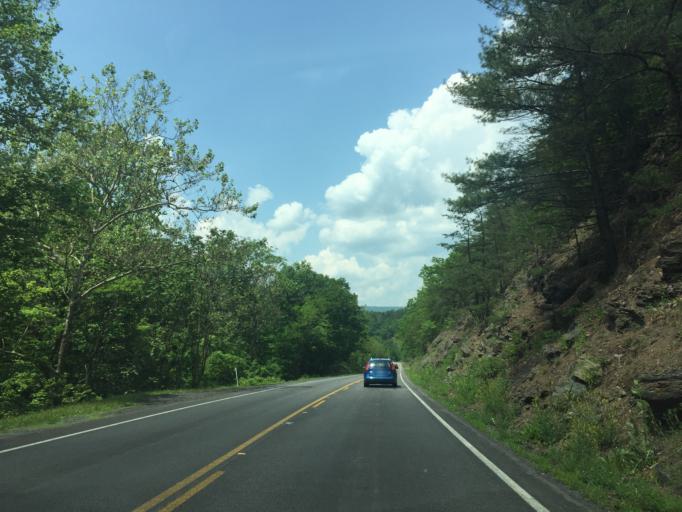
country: US
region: Virginia
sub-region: Shenandoah County
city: Woodstock
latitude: 39.0917
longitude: -78.5592
